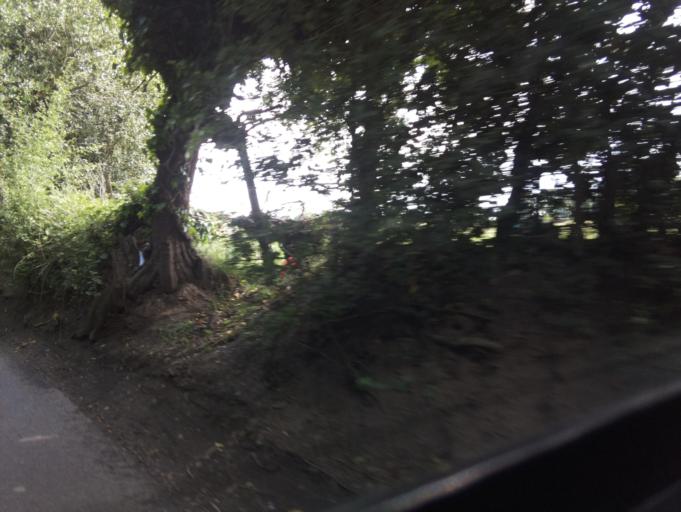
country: GB
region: England
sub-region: Hertfordshire
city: Chorleywood
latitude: 51.6648
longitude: -0.4649
